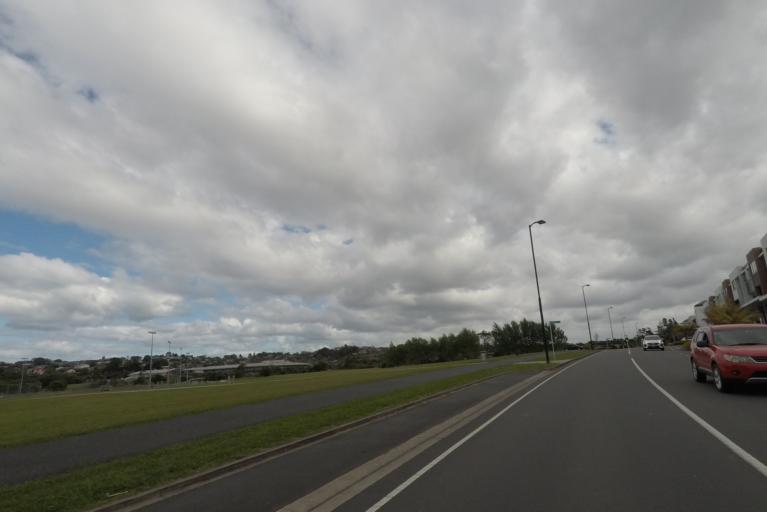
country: NZ
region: Auckland
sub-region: Auckland
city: Rothesay Bay
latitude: -36.6030
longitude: 174.6791
